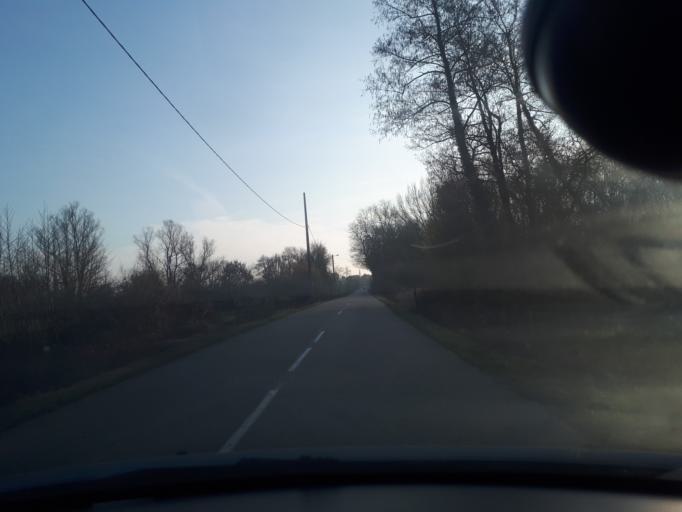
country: FR
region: Rhone-Alpes
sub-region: Departement de l'Isere
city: Creys-Mepieu
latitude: 45.7037
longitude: 5.5342
